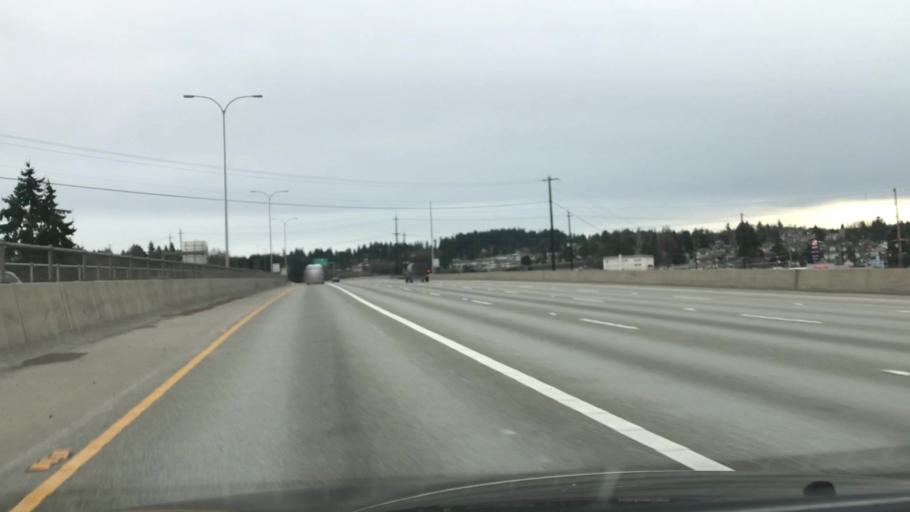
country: US
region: Washington
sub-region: Snohomish County
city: Everett
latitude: 47.9706
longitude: -122.1954
